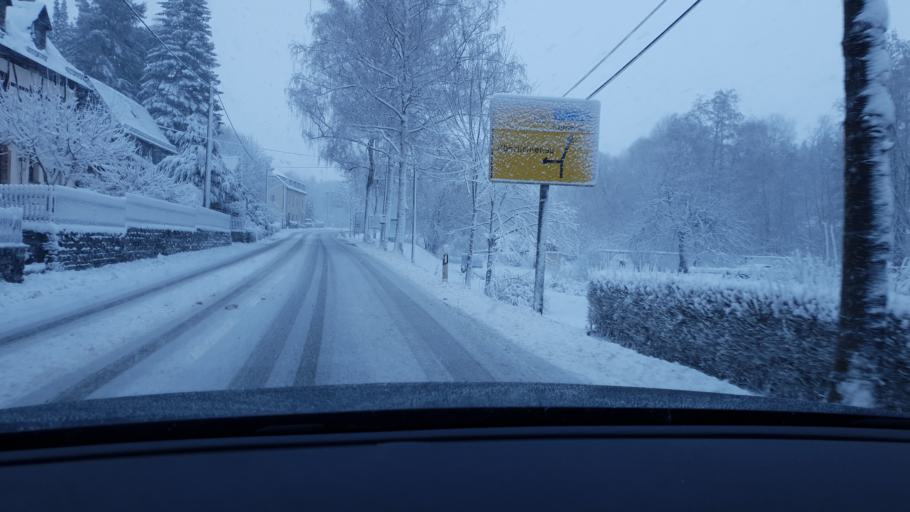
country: DE
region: Saxony
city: Claussnitz
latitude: 50.9040
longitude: 12.9014
